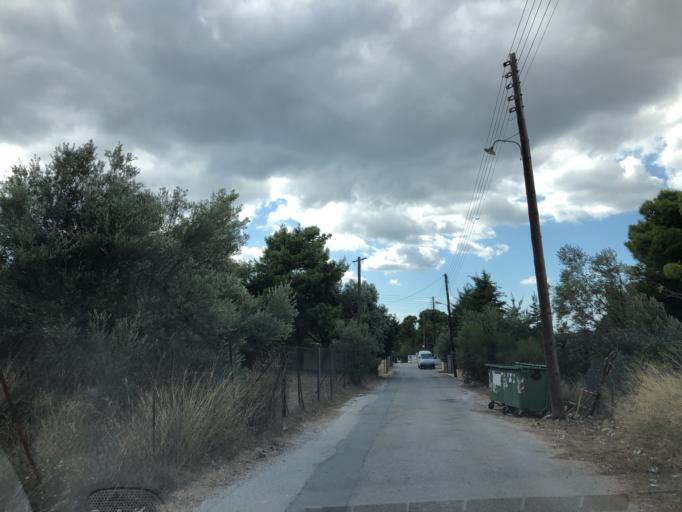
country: GR
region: Attica
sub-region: Nomarchia Anatolikis Attikis
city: Agia Marina
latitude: 37.8233
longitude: 23.8597
